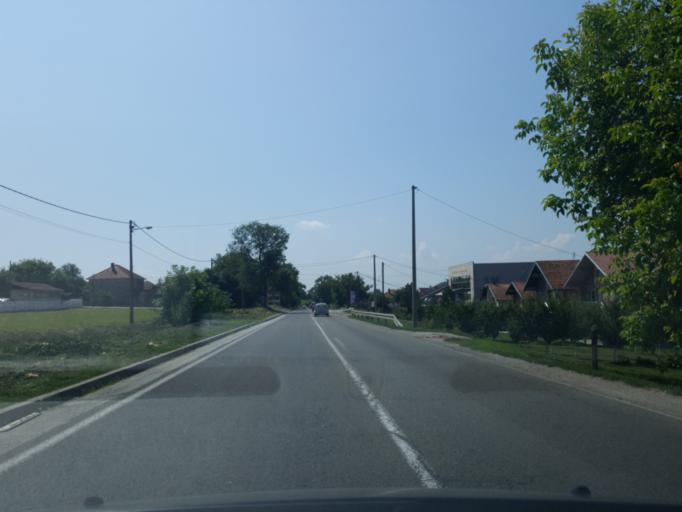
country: RS
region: Central Serbia
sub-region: Belgrade
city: Mladenovac
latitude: 44.4673
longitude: 20.6669
